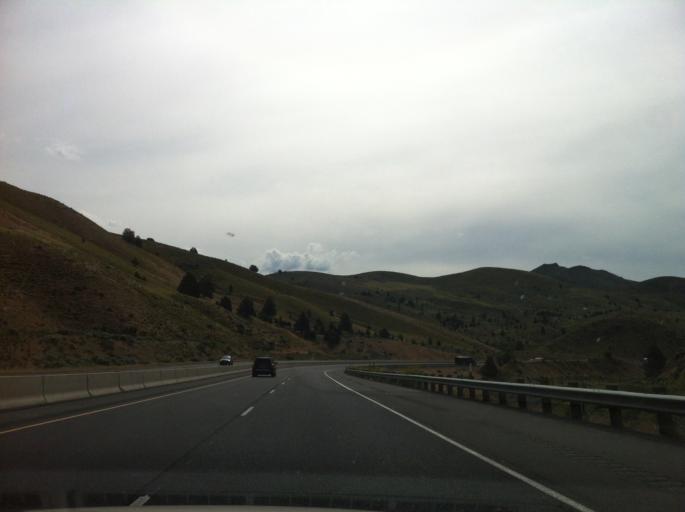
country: US
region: Idaho
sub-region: Washington County
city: Weiser
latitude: 44.5196
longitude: -117.3802
